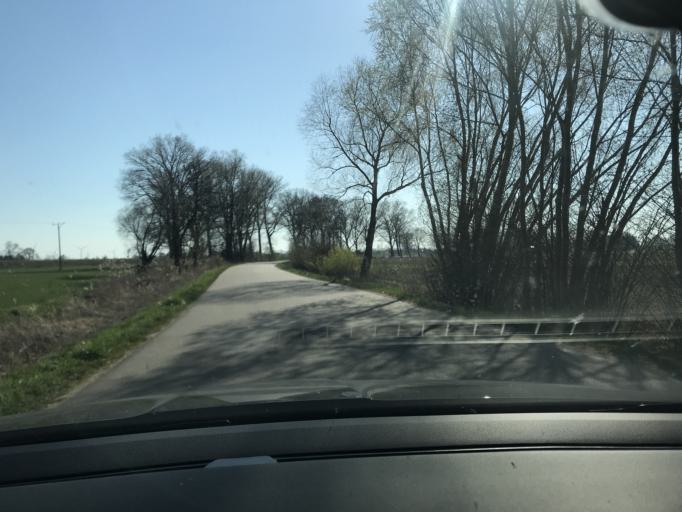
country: PL
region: Pomeranian Voivodeship
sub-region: Powiat nowodworski
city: Stegna
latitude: 54.2951
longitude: 19.1294
